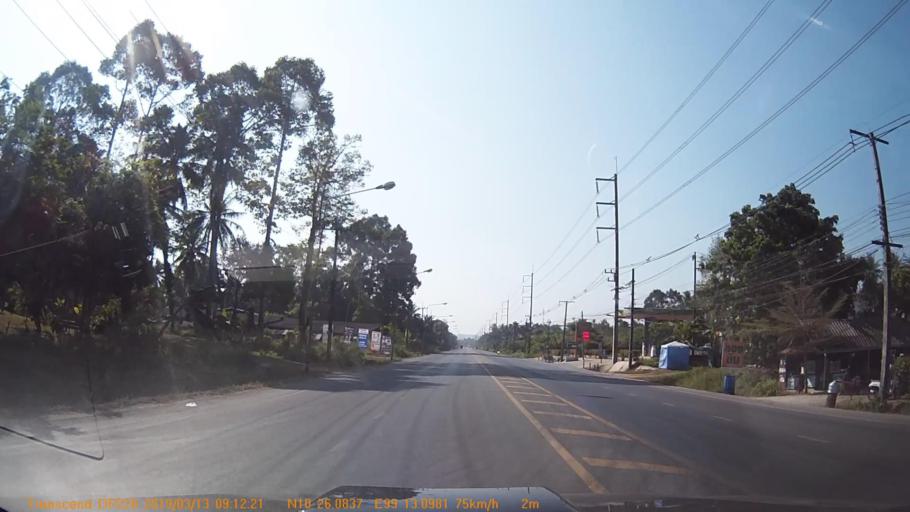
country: TH
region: Chumphon
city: Chumphon
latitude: 10.4346
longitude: 99.2184
